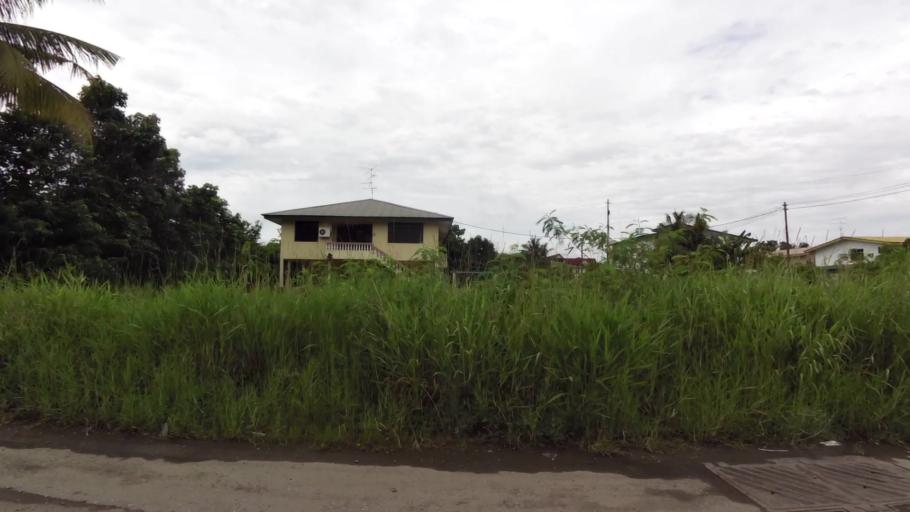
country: BN
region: Brunei and Muara
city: Bandar Seri Begawan
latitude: 4.8970
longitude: 114.9291
